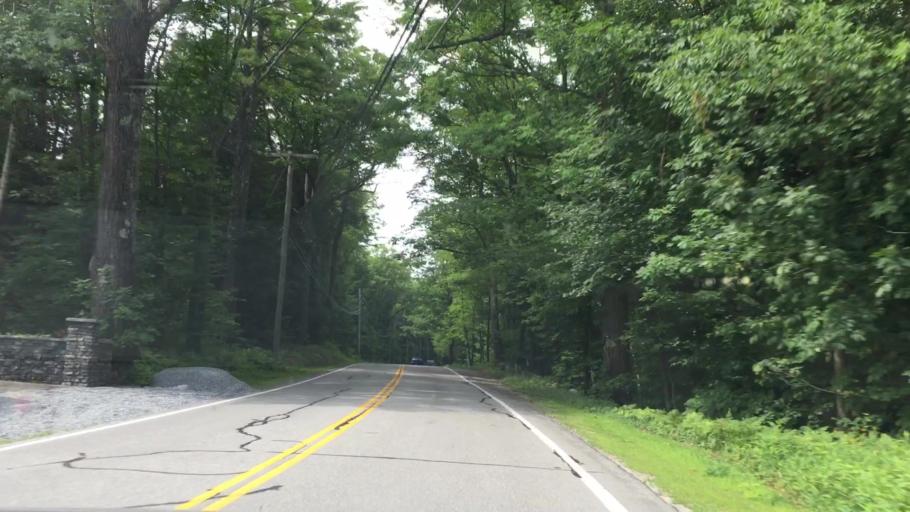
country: US
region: New Hampshire
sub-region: Hillsborough County
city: Antrim
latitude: 43.0367
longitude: -71.9355
